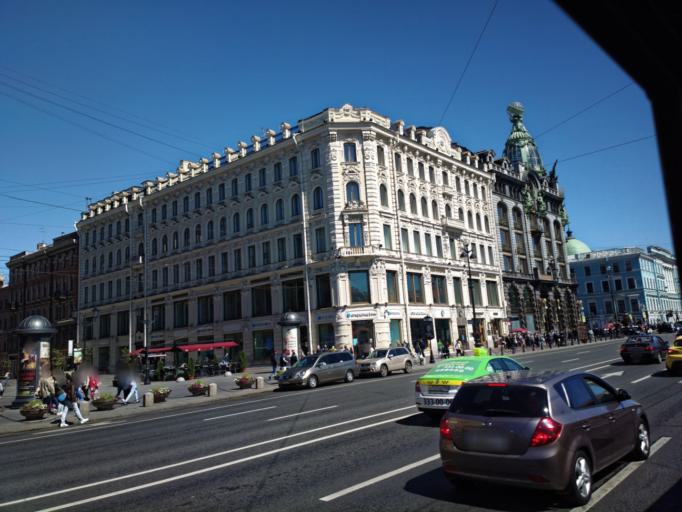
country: RU
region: St.-Petersburg
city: Saint Petersburg
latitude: 59.9355
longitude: 30.3242
